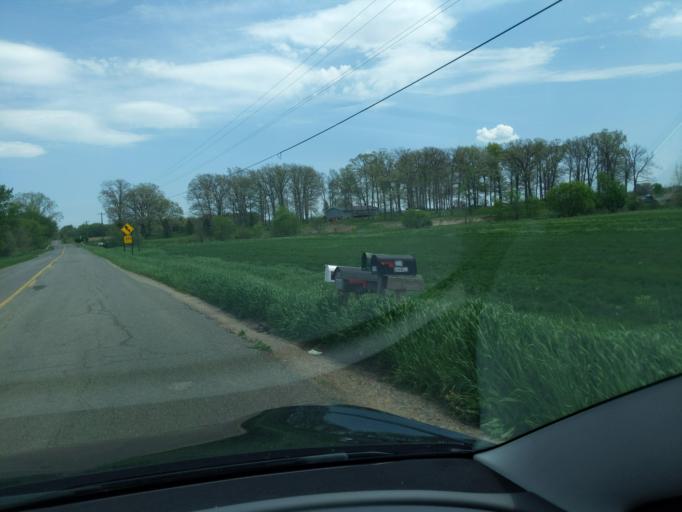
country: US
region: Michigan
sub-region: Ingham County
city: Stockbridge
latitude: 42.4540
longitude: -84.2185
